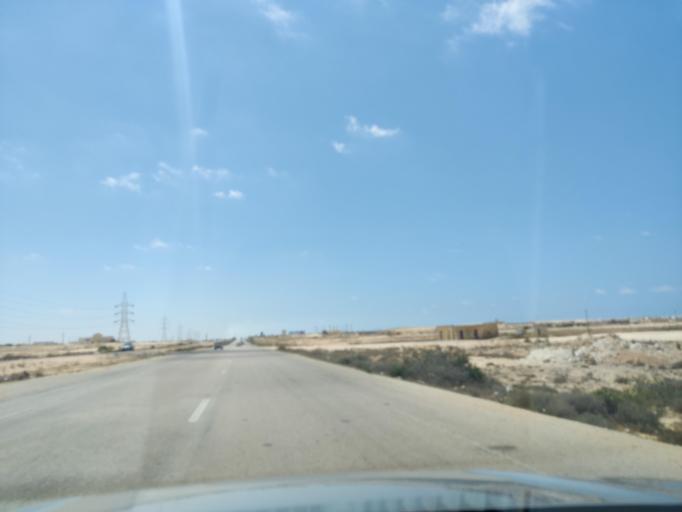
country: EG
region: Muhafazat Matruh
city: Al `Alamayn
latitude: 31.0670
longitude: 28.1773
